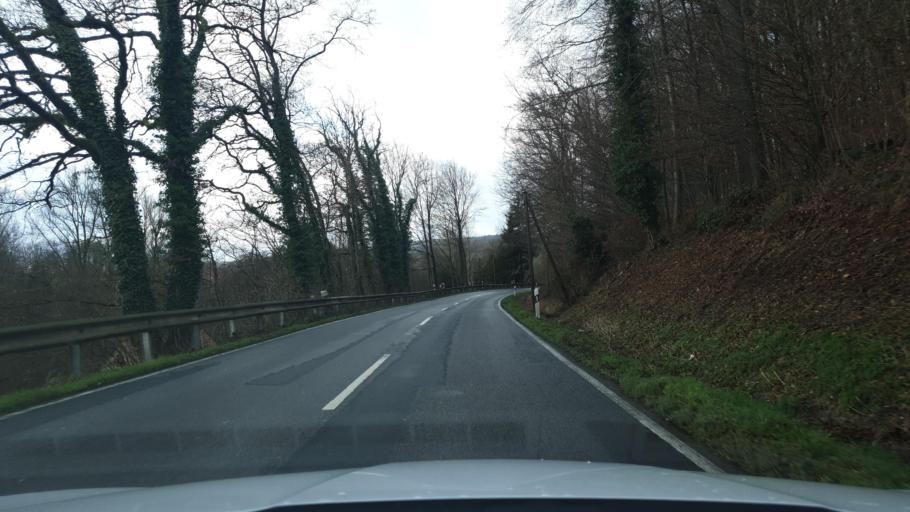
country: DE
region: North Rhine-Westphalia
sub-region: Regierungsbezirk Detmold
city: Bad Salzuflen
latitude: 52.1169
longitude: 8.7715
